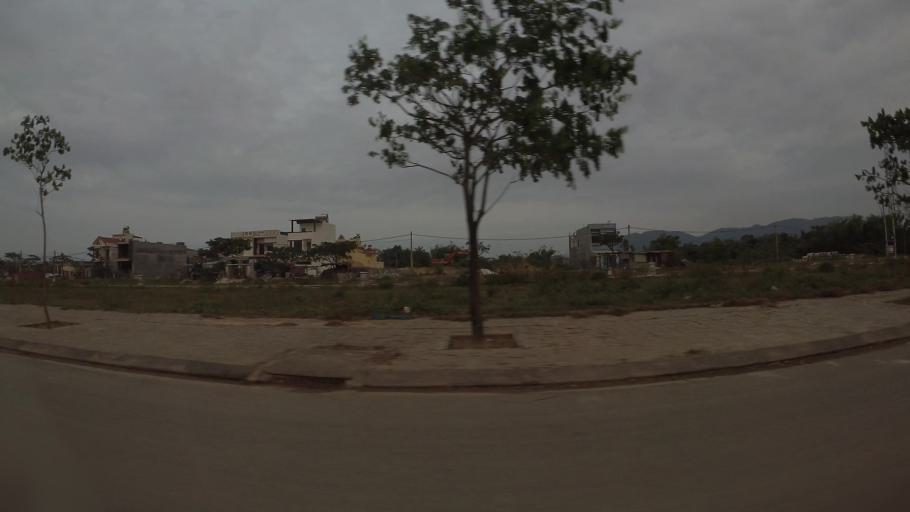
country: VN
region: Da Nang
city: Lien Chieu
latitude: 16.0975
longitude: 108.1137
